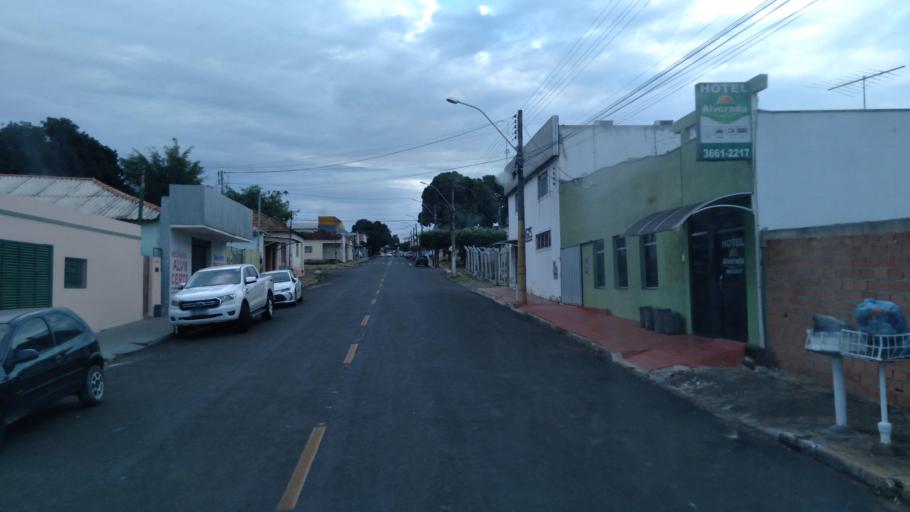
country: BR
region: Goias
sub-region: Mineiros
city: Mineiros
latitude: -17.5654
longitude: -52.5498
